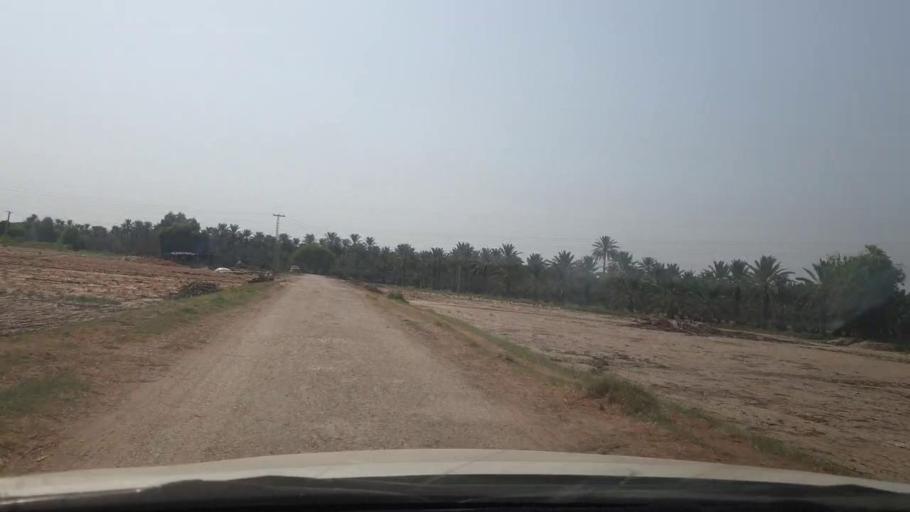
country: PK
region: Sindh
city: Rohri
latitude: 27.5918
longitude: 68.8535
